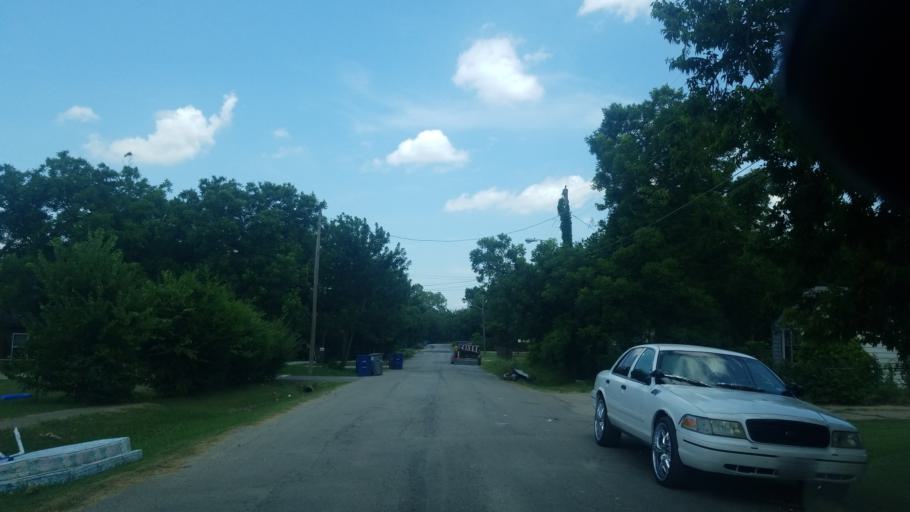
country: US
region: Texas
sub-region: Dallas County
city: Dallas
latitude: 32.7146
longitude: -96.7700
